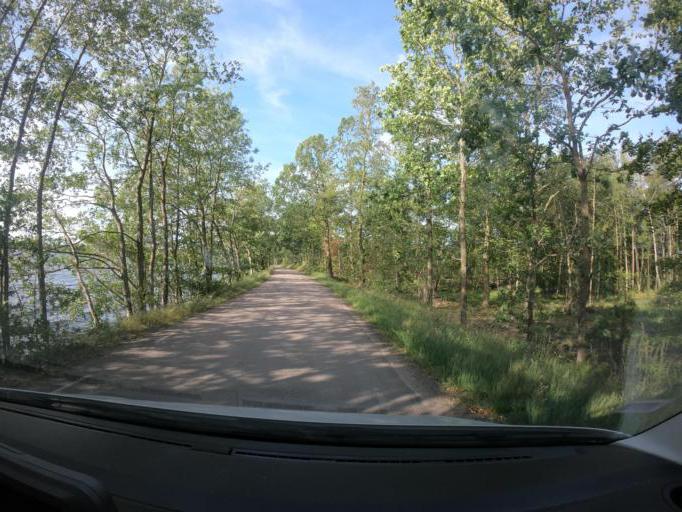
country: SE
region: Skane
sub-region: Angelholms Kommun
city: Munka-Ljungby
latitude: 56.3228
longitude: 13.0713
